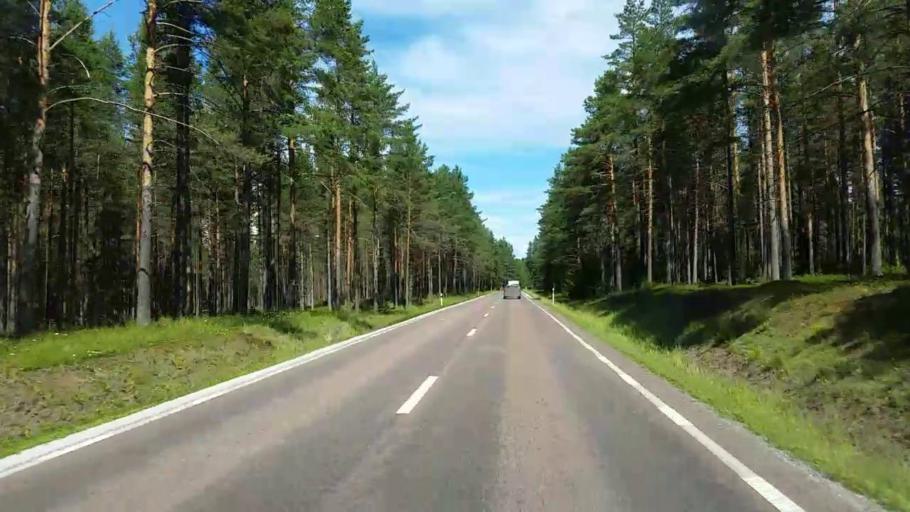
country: SE
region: Dalarna
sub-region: Rattviks Kommun
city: Raettvik
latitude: 60.9140
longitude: 15.2021
